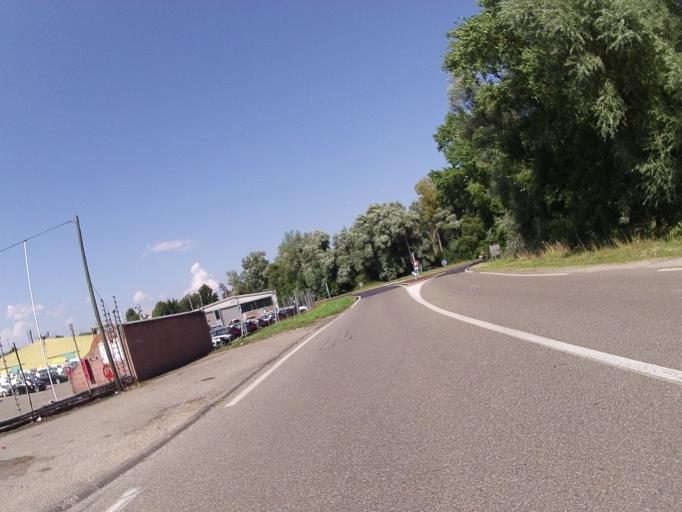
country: DE
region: Rheinland-Pfalz
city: Berg
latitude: 48.9647
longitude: 8.1842
